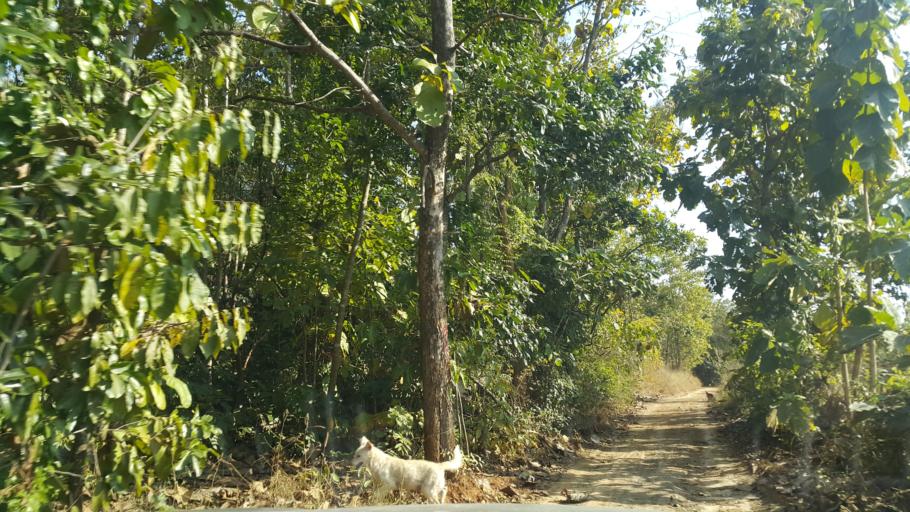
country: TH
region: Lamphun
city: Mae Tha
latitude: 18.5315
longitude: 99.1056
